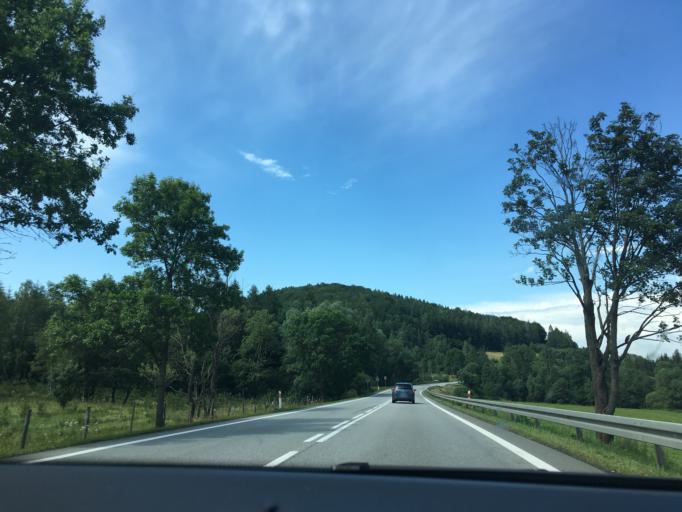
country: PL
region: Subcarpathian Voivodeship
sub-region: Powiat krosnienski
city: Dukla
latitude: 49.4428
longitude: 21.6904
